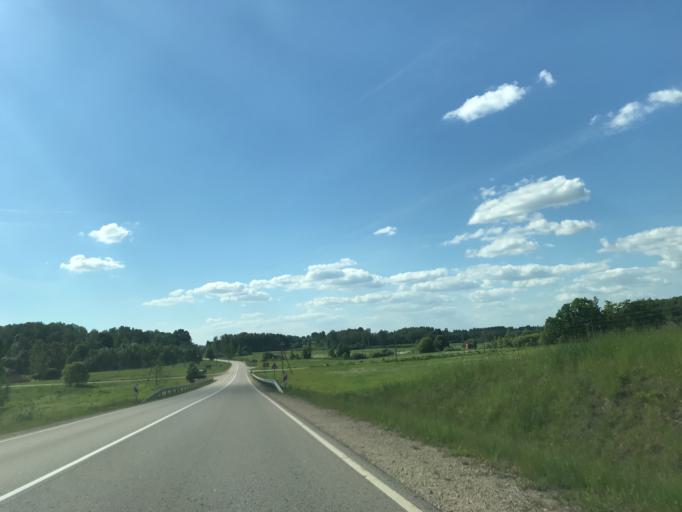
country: LV
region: Plavinu
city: Plavinas
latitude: 56.5597
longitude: 25.6435
